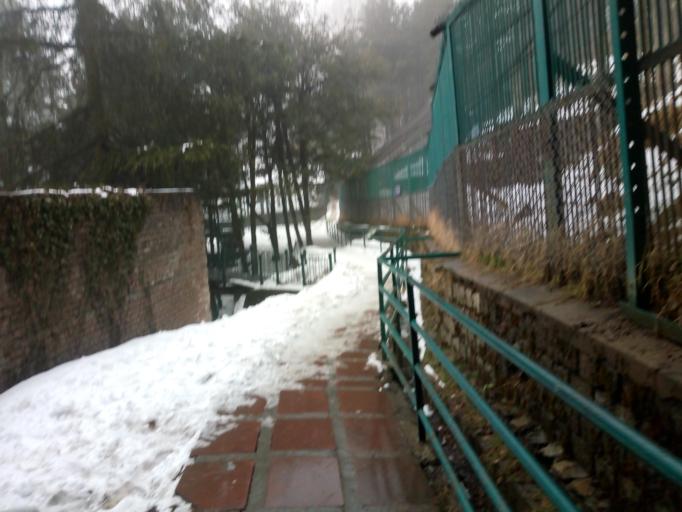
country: IN
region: Himachal Pradesh
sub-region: Shimla
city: Shimla
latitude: 31.0960
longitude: 77.2636
